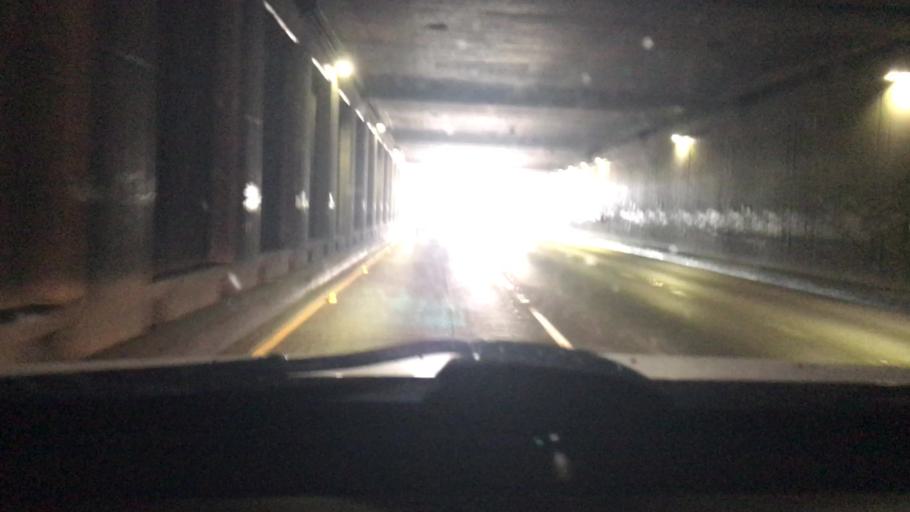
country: US
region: California
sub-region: Los Angeles County
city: El Segundo
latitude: 33.9388
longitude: -118.3961
